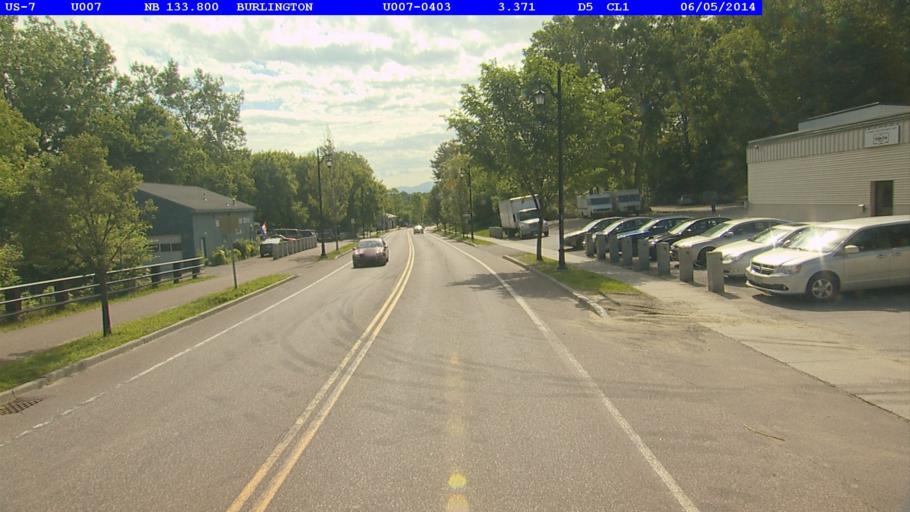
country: US
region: Vermont
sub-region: Chittenden County
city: Winooski
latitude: 44.4882
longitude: -73.1994
